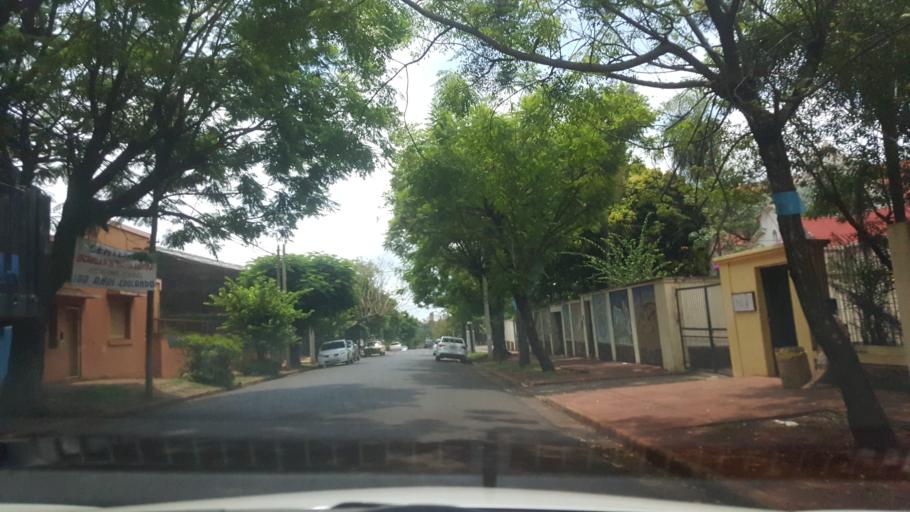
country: AR
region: Misiones
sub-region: Departamento de Capital
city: Posadas
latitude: -27.3858
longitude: -55.8944
